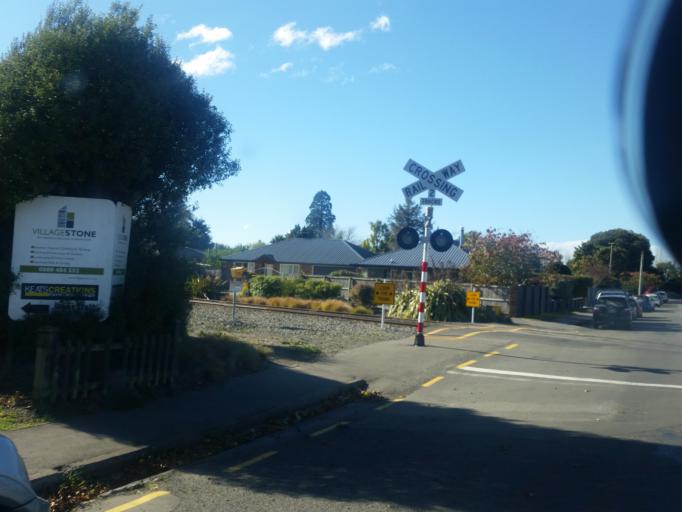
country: NZ
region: Canterbury
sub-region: Waimakariri District
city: Woodend
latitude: -43.2966
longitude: 172.5966
